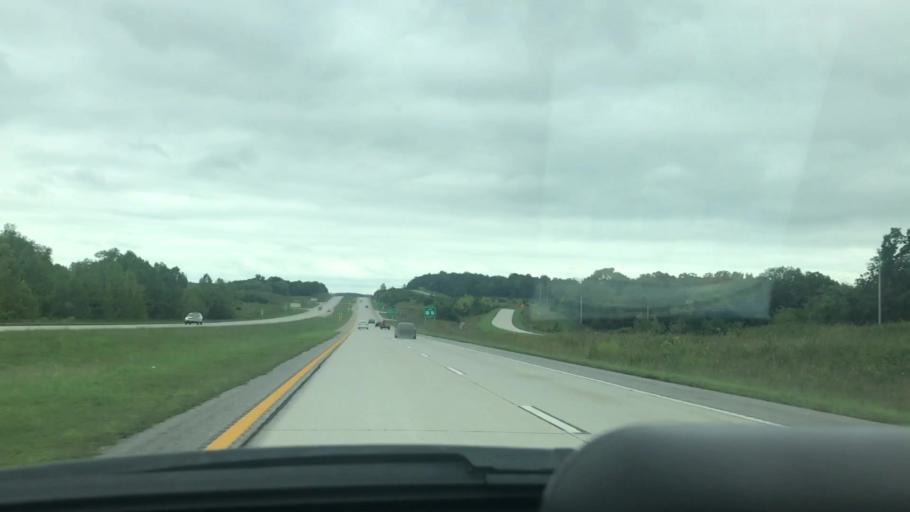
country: US
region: Missouri
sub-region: Greene County
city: Fair Grove
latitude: 37.5124
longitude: -93.1387
